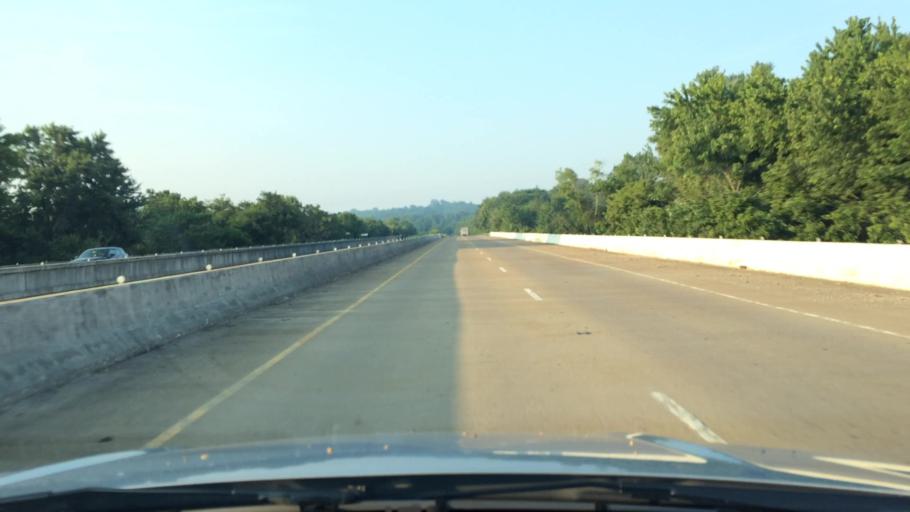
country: US
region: Tennessee
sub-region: Giles County
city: Pulaski
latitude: 35.1960
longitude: -87.0640
